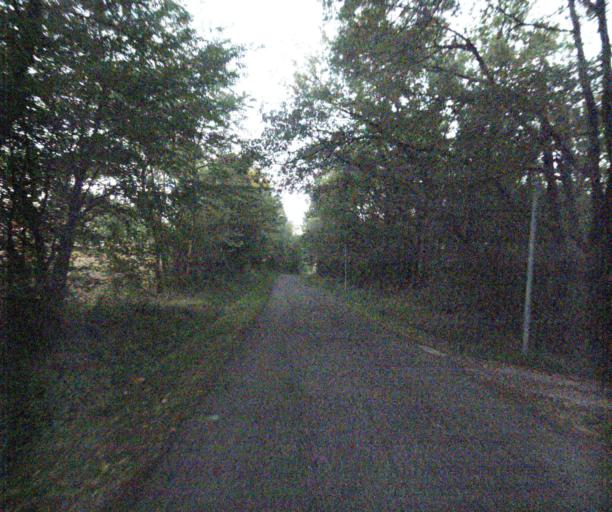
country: FR
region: Midi-Pyrenees
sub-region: Departement du Gers
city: Vic-Fezensac
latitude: 43.7841
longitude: 0.2230
